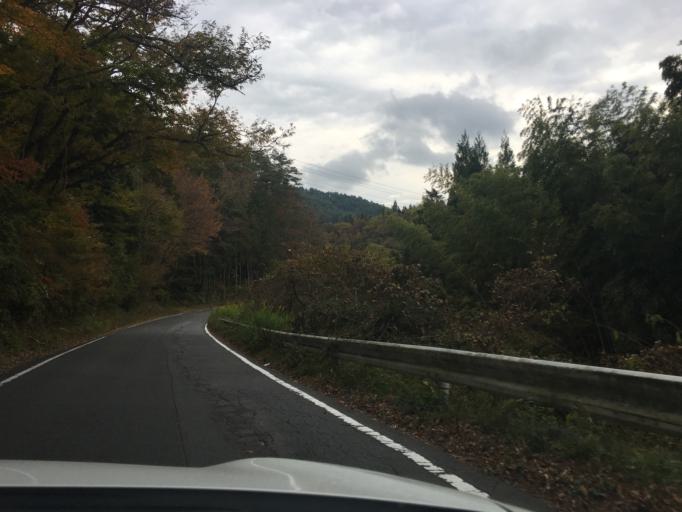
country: JP
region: Fukushima
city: Iwaki
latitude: 37.1304
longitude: 140.7753
